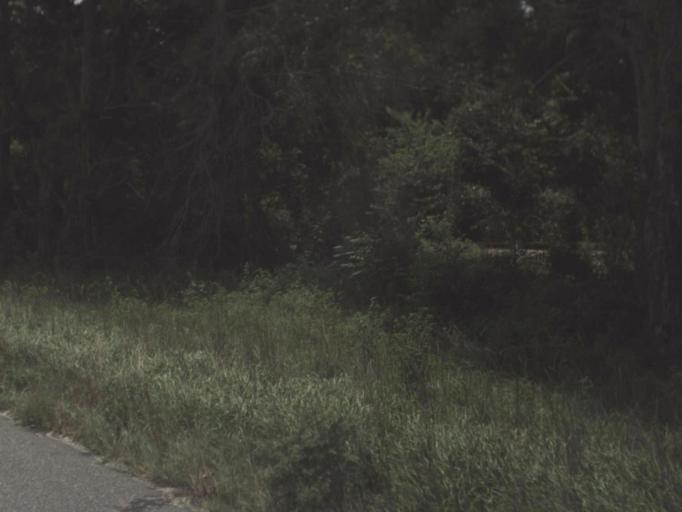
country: US
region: Florida
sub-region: Madison County
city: Madison
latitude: 30.4091
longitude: -83.2574
